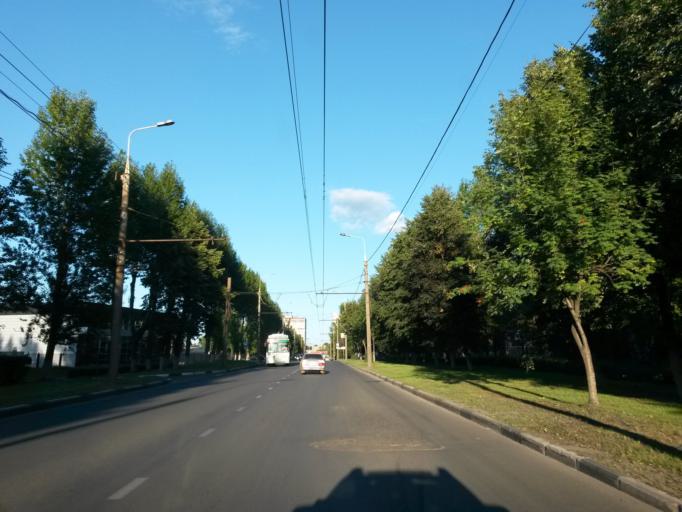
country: RU
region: Jaroslavl
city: Yaroslavl
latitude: 57.5904
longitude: 39.8525
